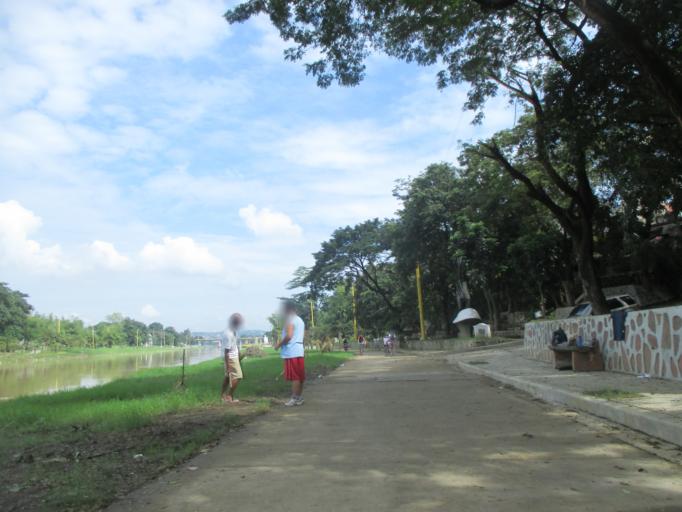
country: PH
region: Metro Manila
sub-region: Marikina
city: Calumpang
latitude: 14.6284
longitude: 121.0945
